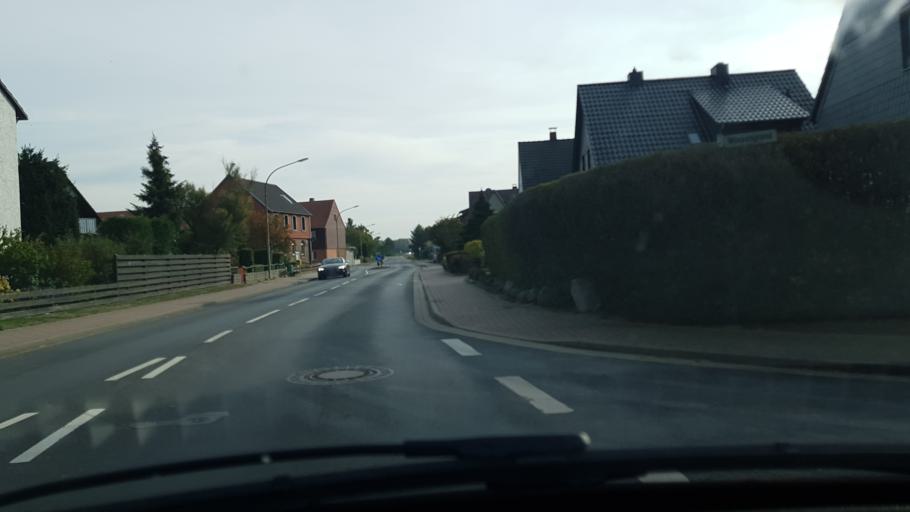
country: DE
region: Lower Saxony
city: Lehre
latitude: 52.3065
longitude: 10.6586
